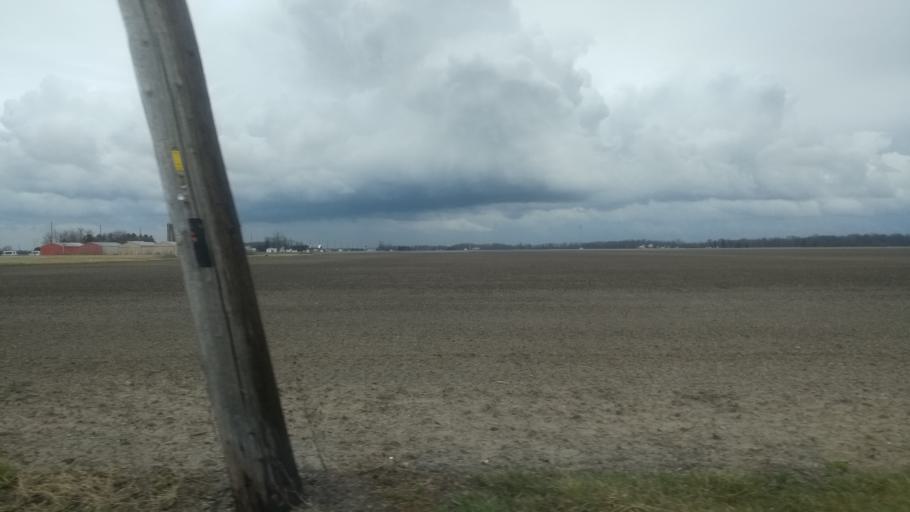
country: US
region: Ohio
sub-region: Wood County
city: Bowling Green
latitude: 41.3716
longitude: -83.6102
